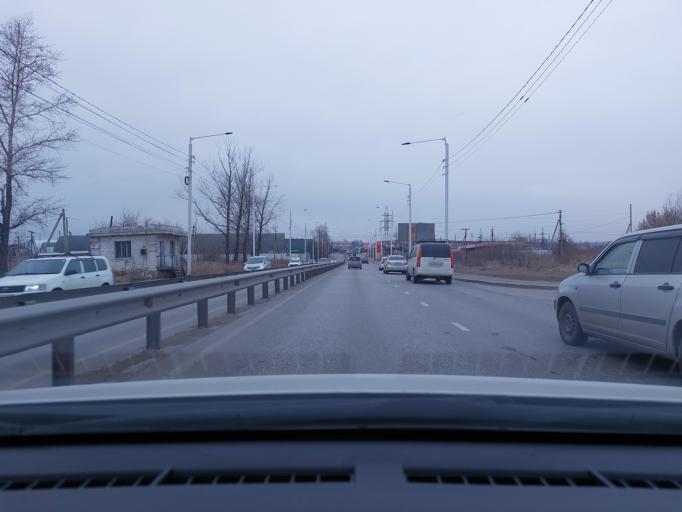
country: RU
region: Irkutsk
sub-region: Irkutskiy Rayon
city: Irkutsk
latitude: 52.3343
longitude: 104.2333
